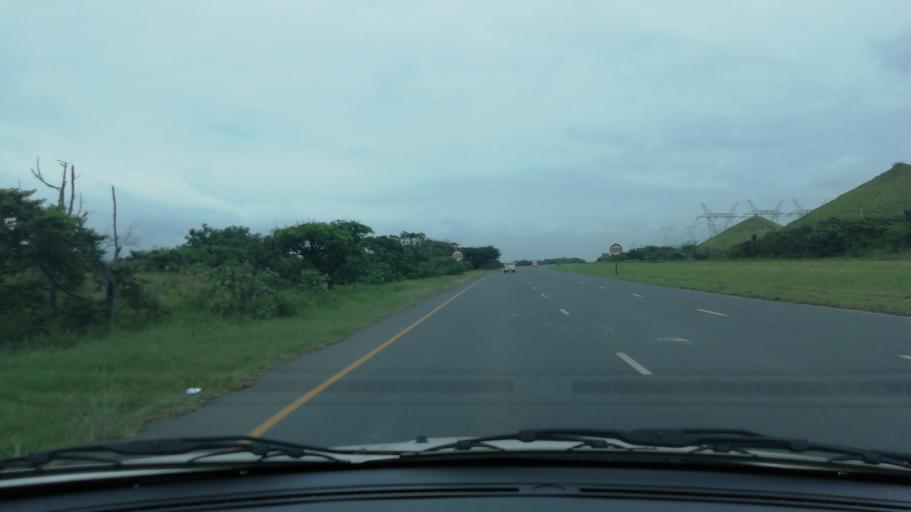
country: ZA
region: KwaZulu-Natal
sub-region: uThungulu District Municipality
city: Richards Bay
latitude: -28.7717
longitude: 32.0284
